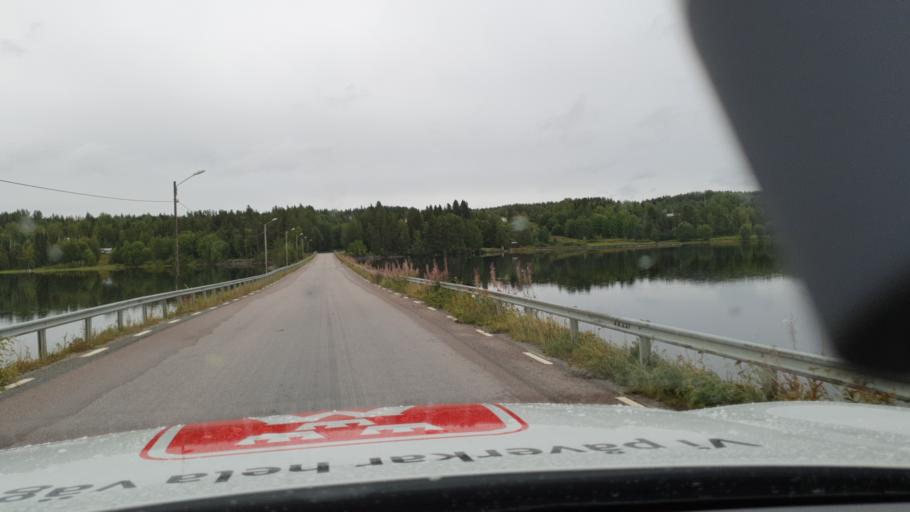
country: SE
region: Jaemtland
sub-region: Stroemsunds Kommun
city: Stroemsund
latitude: 64.4364
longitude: 15.5762
